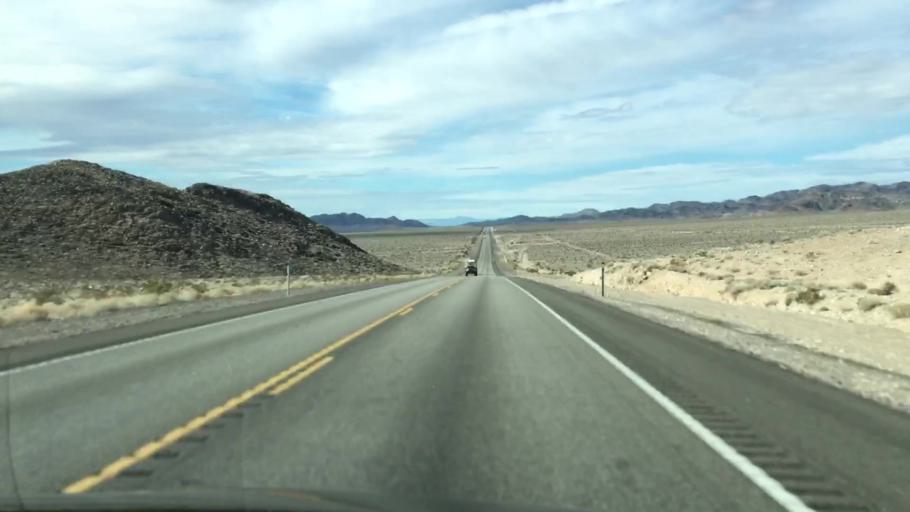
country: US
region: Nevada
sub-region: Nye County
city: Pahrump
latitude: 36.5823
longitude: -116.2057
